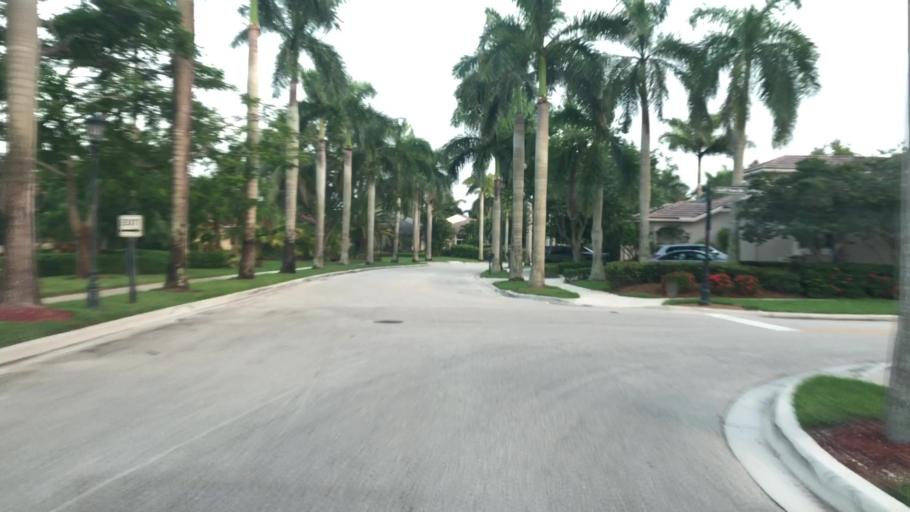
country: US
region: Florida
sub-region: Broward County
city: Weston
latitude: 26.1007
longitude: -80.4000
